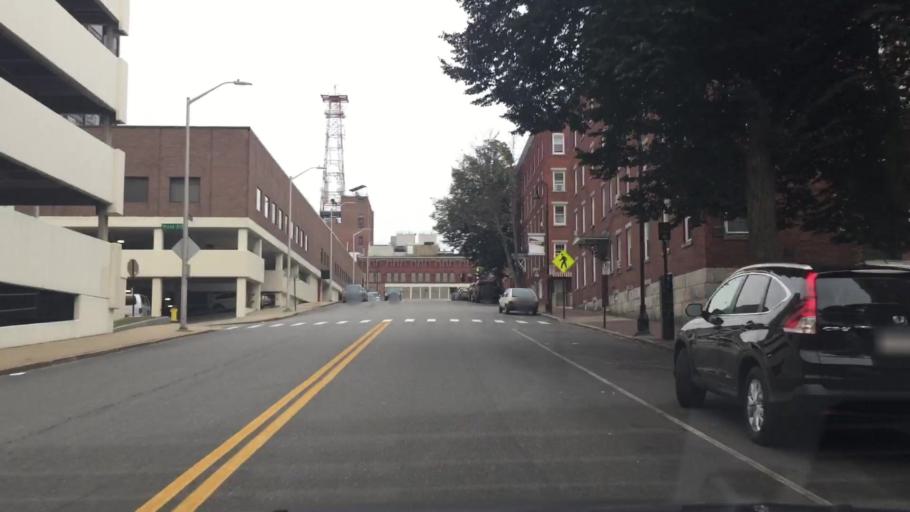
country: US
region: New Hampshire
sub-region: Hillsborough County
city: Manchester
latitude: 42.9922
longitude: -71.4659
